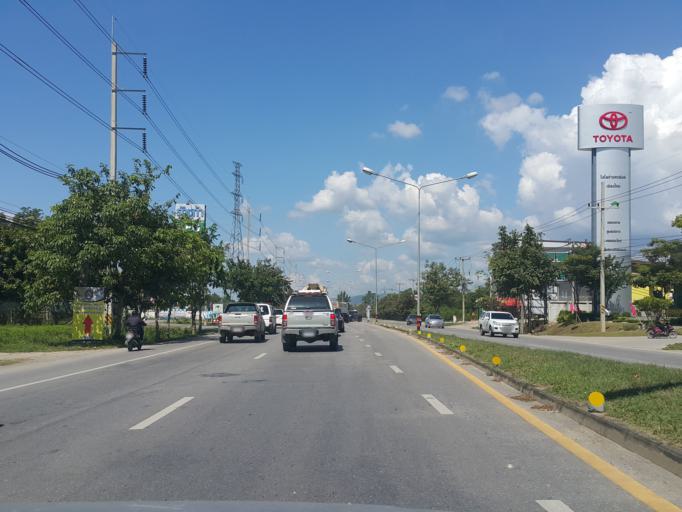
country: TH
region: Chiang Mai
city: San Sai
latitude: 18.8558
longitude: 99.0143
